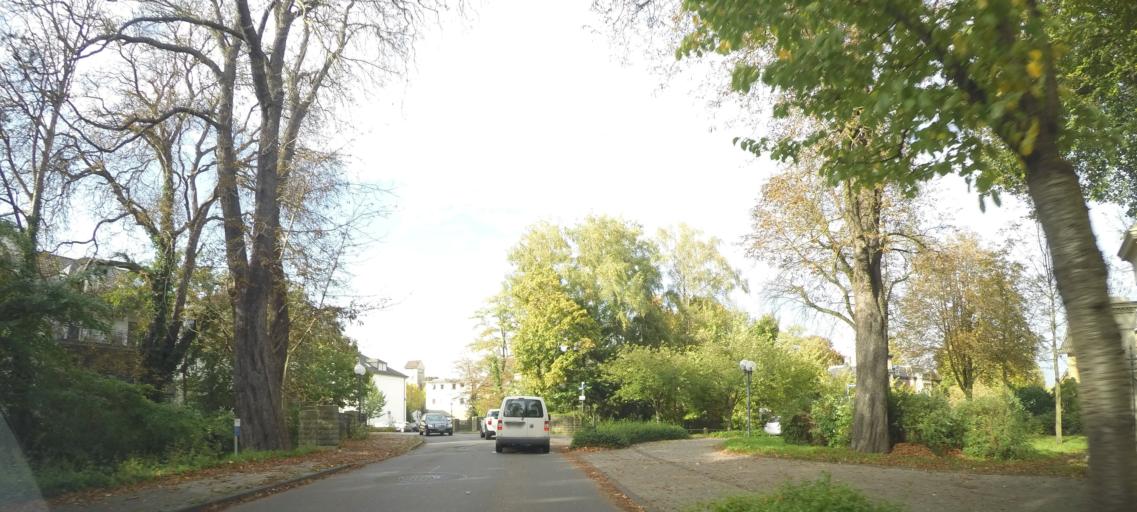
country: DE
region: North Rhine-Westphalia
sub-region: Regierungsbezirk Arnsberg
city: Lippstadt
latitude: 51.6729
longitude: 8.3527
